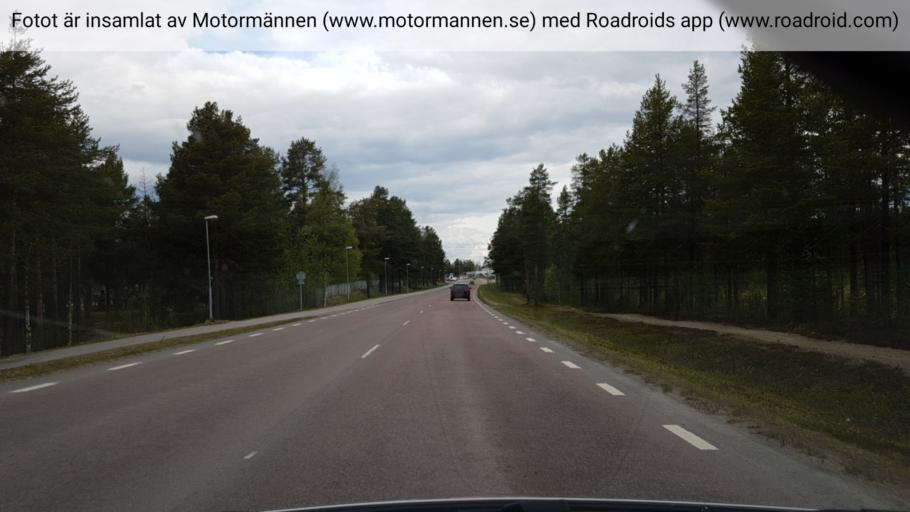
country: SE
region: Norrbotten
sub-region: Arvidsjaurs Kommun
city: Arvidsjaur
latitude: 65.5824
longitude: 19.2038
